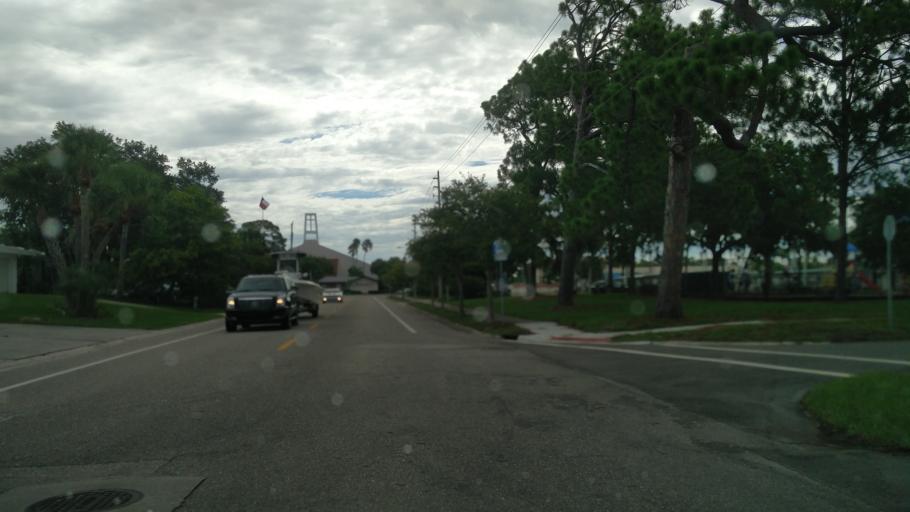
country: US
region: Florida
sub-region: Sarasota County
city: Venice
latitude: 27.1011
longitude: -82.4517
